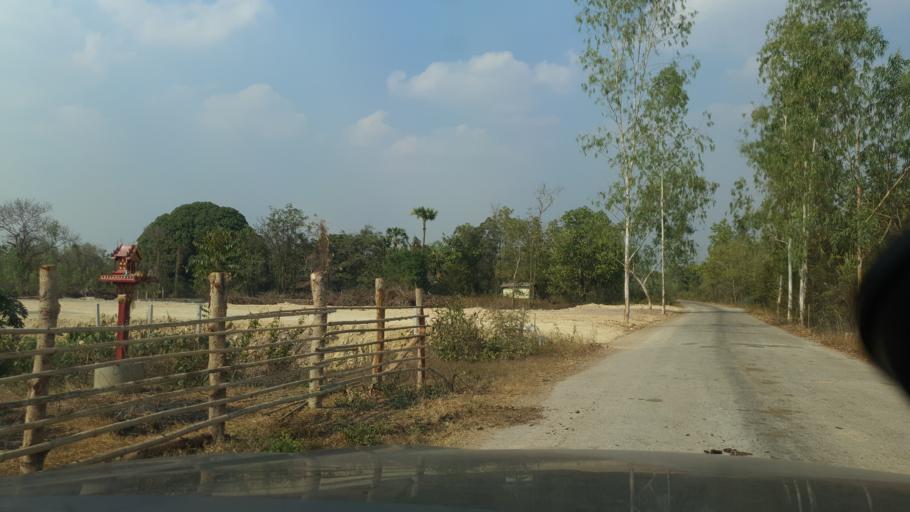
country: TH
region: Sukhothai
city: Ban Dan Lan Hoi
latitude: 17.0136
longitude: 99.5582
